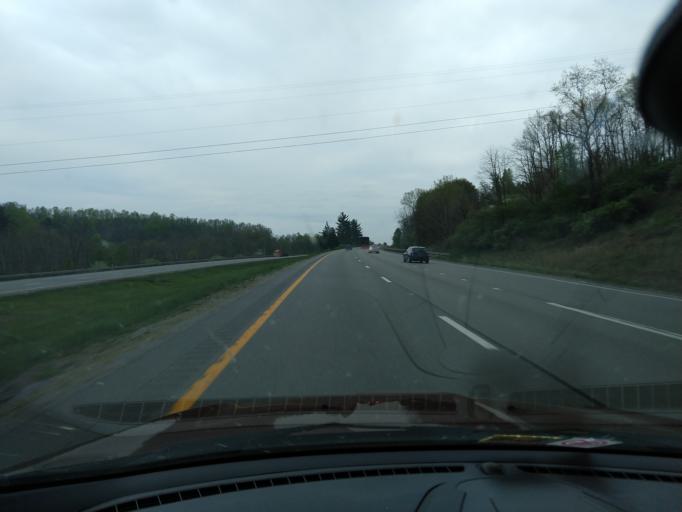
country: US
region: West Virginia
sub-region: Lewis County
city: Weston
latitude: 39.1087
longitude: -80.3916
